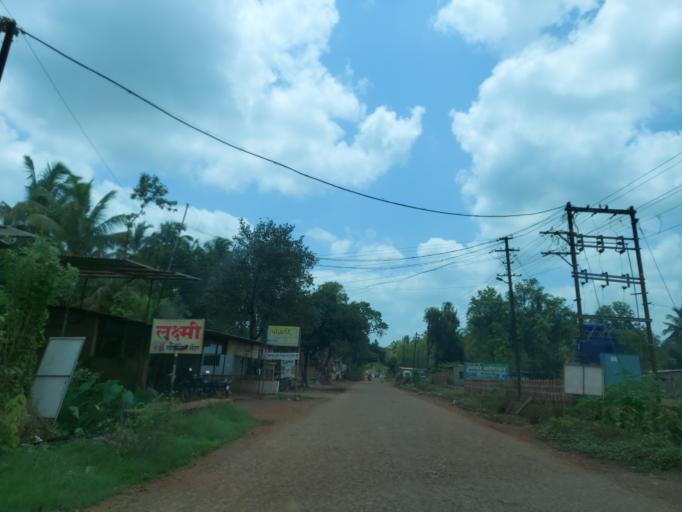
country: IN
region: Maharashtra
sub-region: Sindhudurg
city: Savantvadi
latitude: 15.8202
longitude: 73.8699
